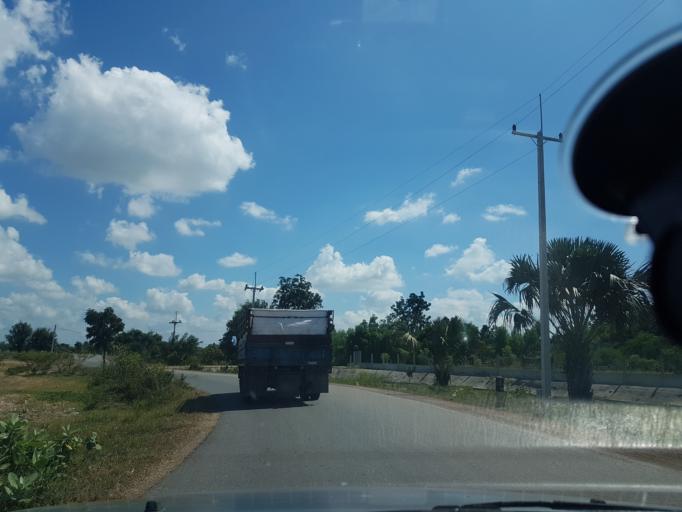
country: TH
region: Lop Buri
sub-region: Amphoe Tha Luang
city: Tha Luang
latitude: 14.9876
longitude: 101.0120
